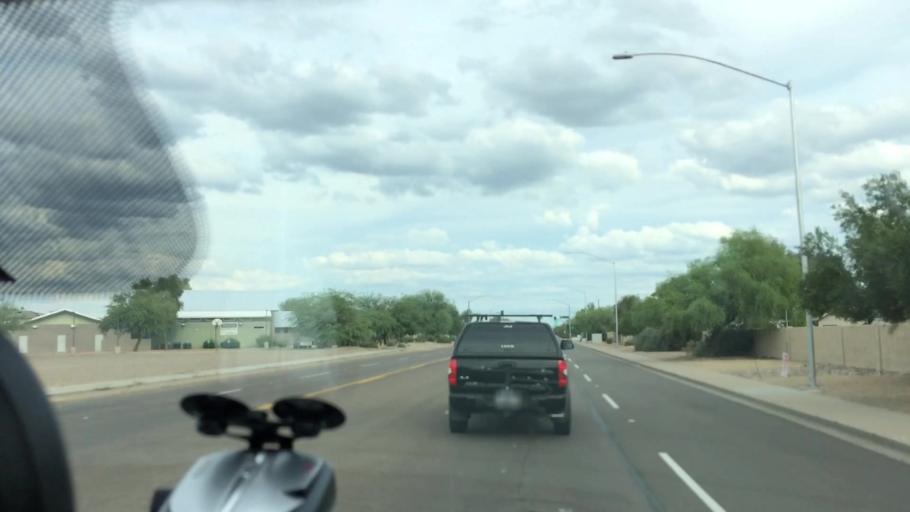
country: US
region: Arizona
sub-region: Maricopa County
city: Peoria
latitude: 33.5664
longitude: -112.2486
